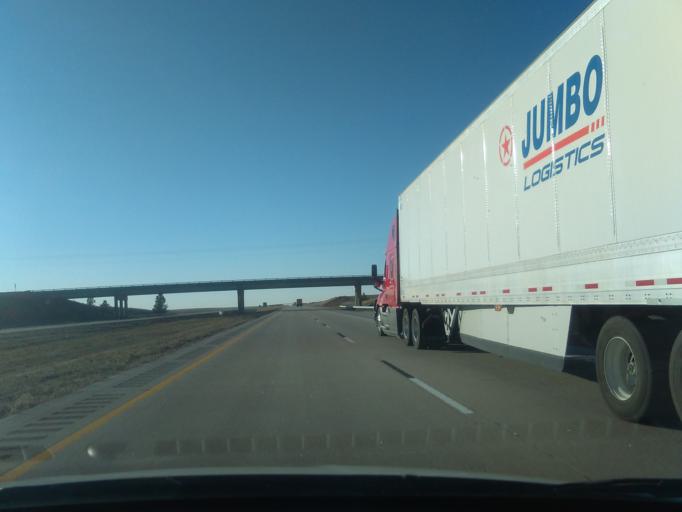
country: US
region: Nebraska
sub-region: Deuel County
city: Chappell
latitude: 41.1134
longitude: -102.6846
